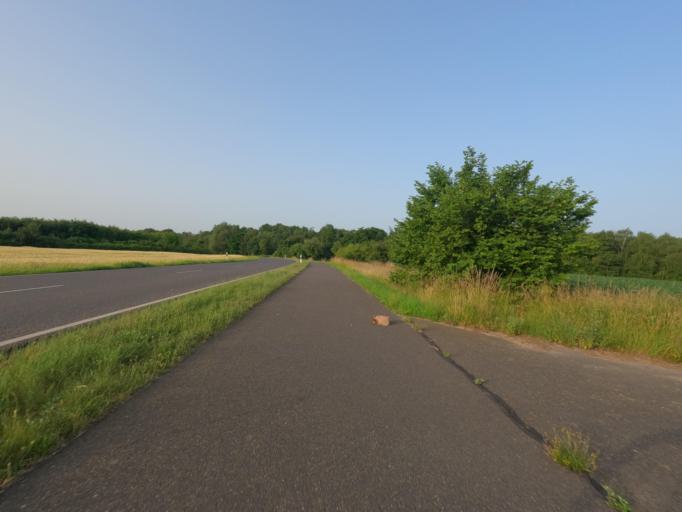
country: DE
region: North Rhine-Westphalia
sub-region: Regierungsbezirk Koln
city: Wassenberg
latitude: 51.0871
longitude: 6.1865
